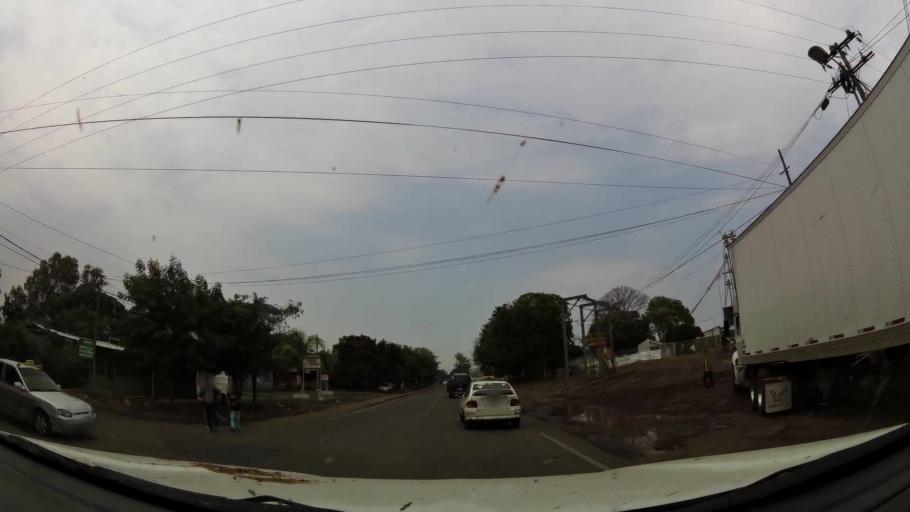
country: NI
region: Masaya
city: Masaya
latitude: 11.9710
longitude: -86.0813
